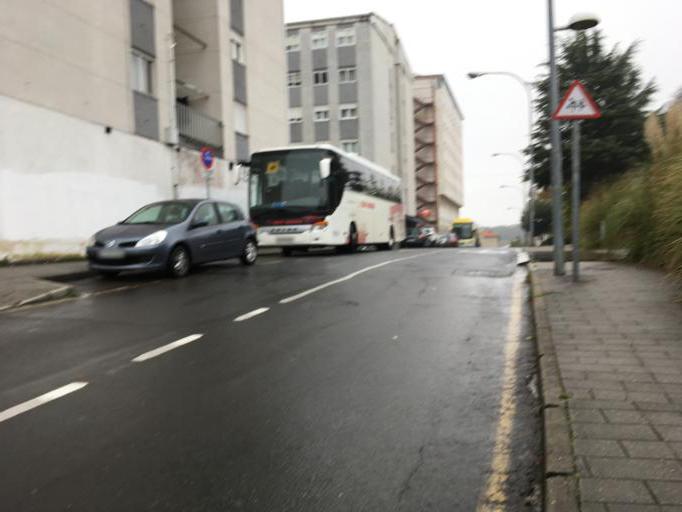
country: ES
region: Galicia
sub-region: Provincia da Coruna
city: Santiago de Compostela
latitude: 42.8706
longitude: -8.5544
